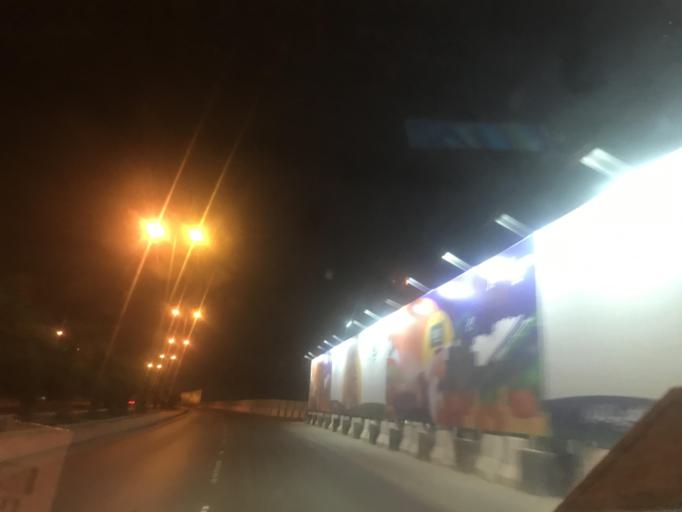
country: SA
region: Ar Riyad
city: Riyadh
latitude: 24.7847
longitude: 46.5914
